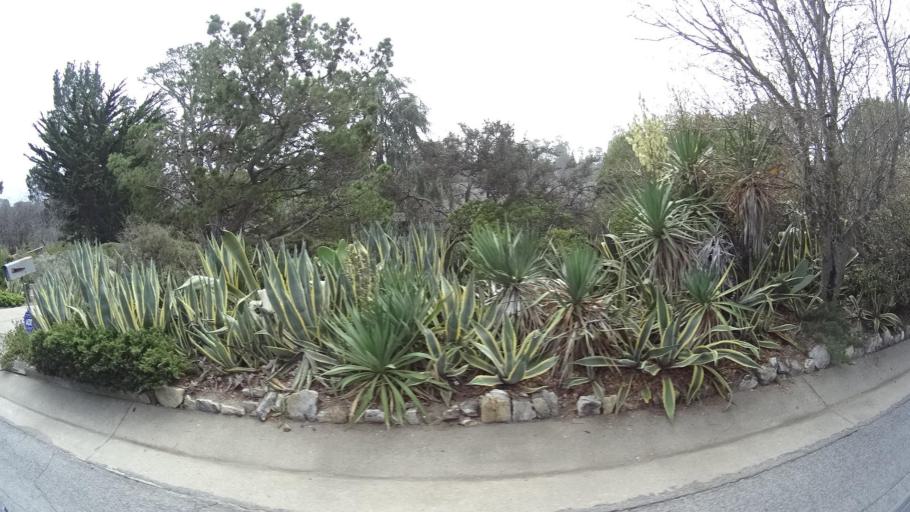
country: US
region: California
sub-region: Monterey County
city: Carmel-by-the-Sea
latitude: 36.5589
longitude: -121.9000
